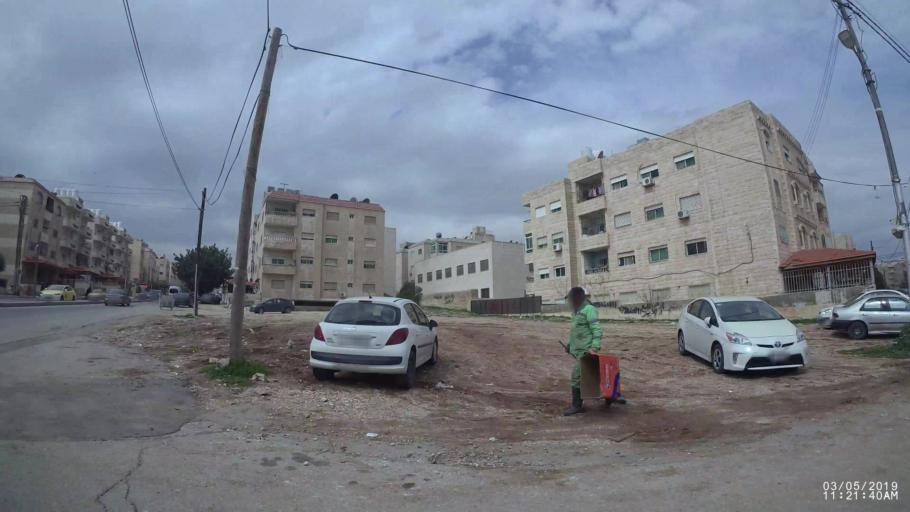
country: JO
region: Amman
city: Amman
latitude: 31.9874
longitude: 35.9281
